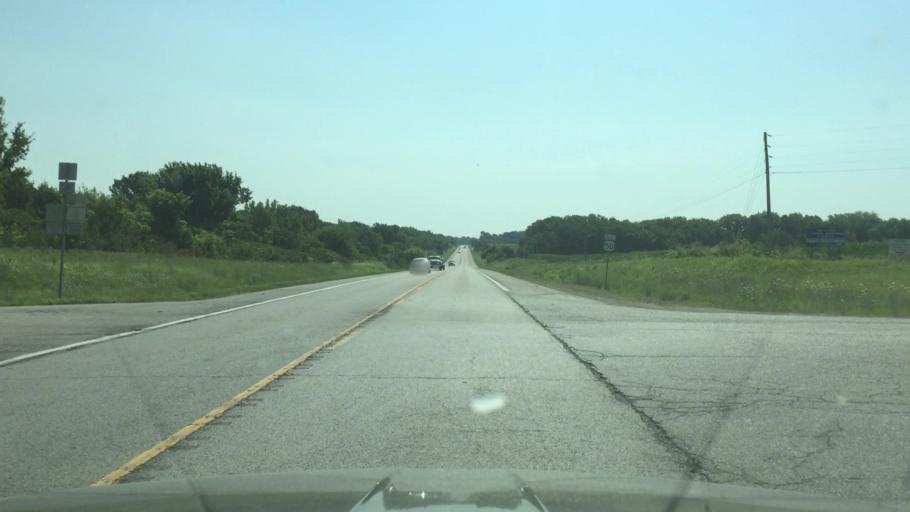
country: US
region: Missouri
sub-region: Pettis County
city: Sedalia
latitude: 38.6937
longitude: -93.0974
